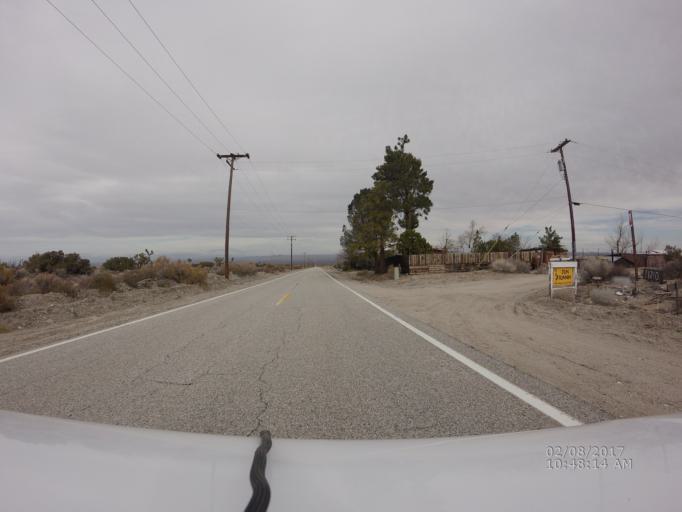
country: US
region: California
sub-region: San Bernardino County
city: Pinon Hills
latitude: 34.4621
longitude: -117.7651
